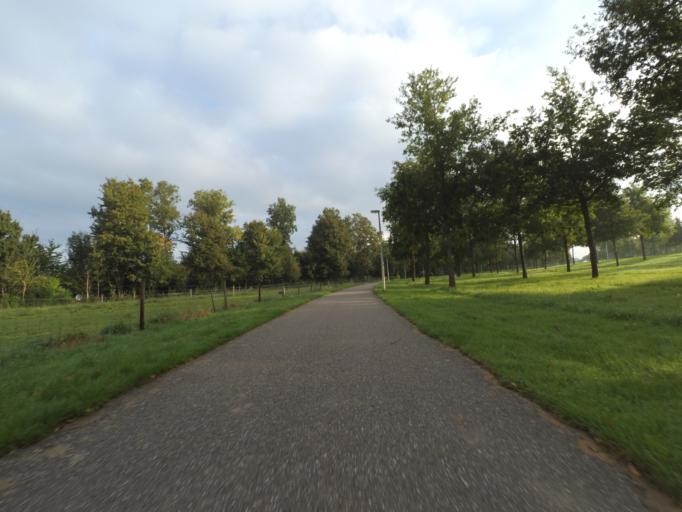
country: NL
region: Flevoland
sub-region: Gemeente Dronten
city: Dronten
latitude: 52.5199
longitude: 5.6902
